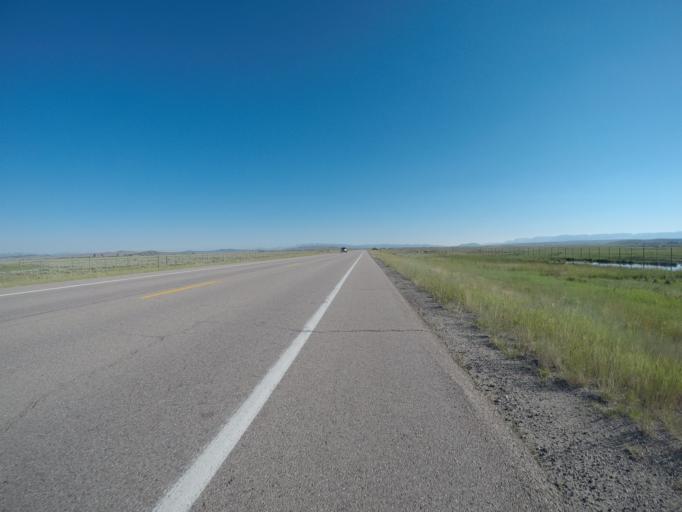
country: US
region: Wyoming
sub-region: Sublette County
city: Pinedale
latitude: 42.9533
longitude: -110.0865
